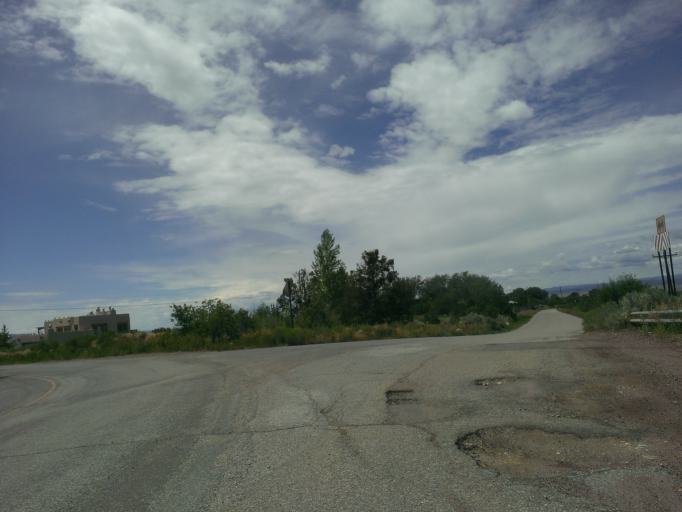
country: US
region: New Mexico
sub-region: Taos County
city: Arroyo Seco
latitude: 36.5321
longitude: -105.5724
